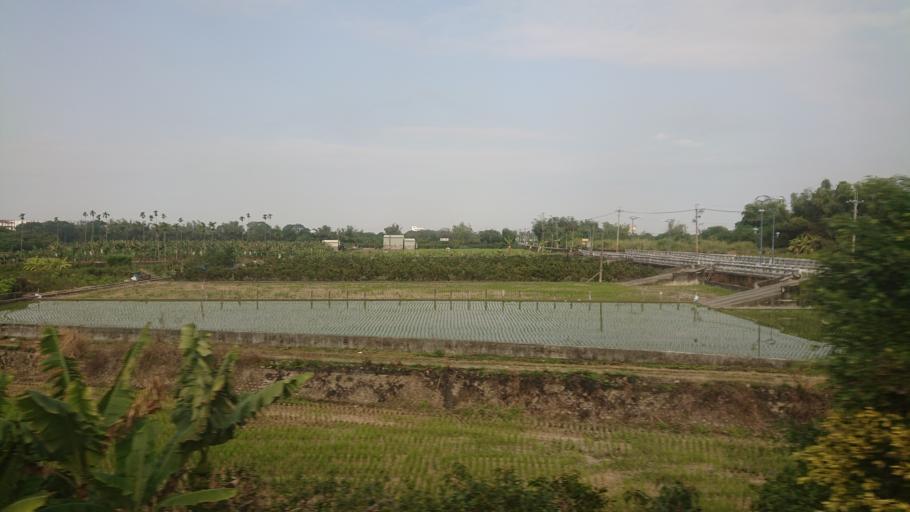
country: TW
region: Taiwan
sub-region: Yunlin
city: Douliu
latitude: 23.7268
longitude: 120.5749
